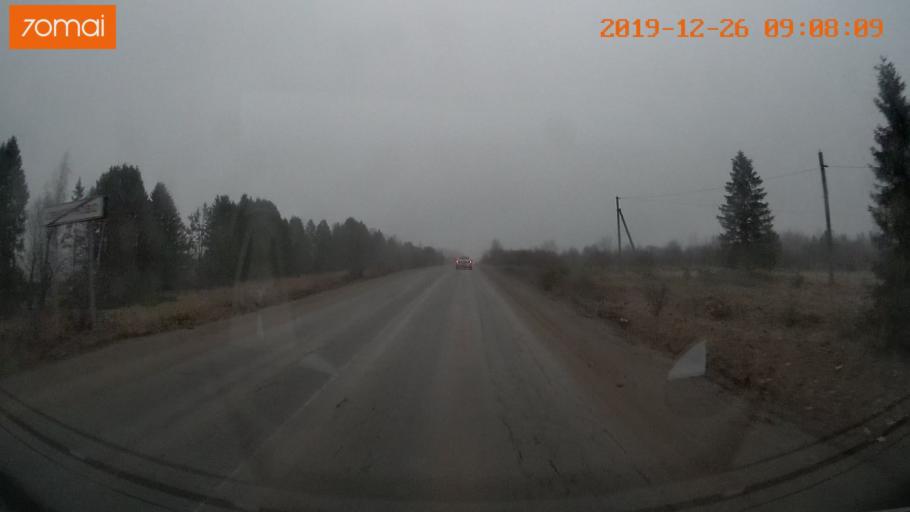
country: RU
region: Vologda
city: Gryazovets
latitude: 58.8538
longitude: 40.2476
